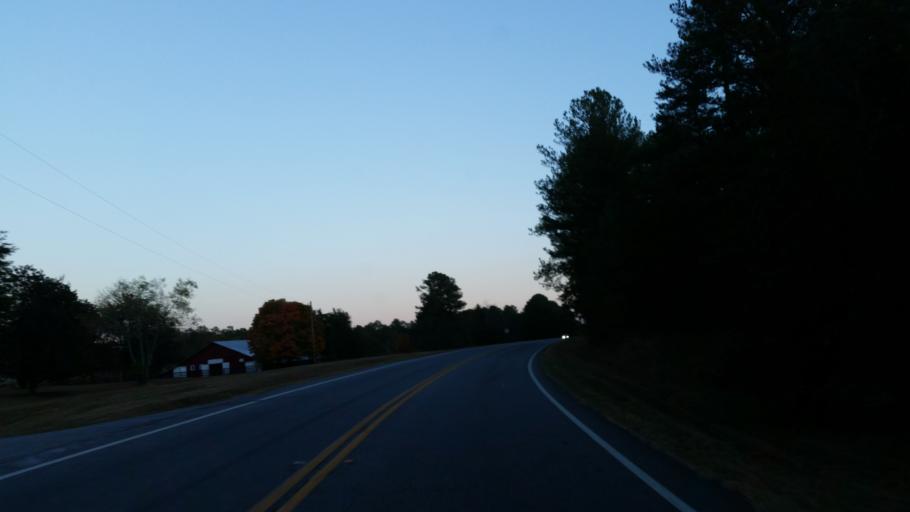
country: US
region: Georgia
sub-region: Gordon County
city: Calhoun
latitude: 34.5881
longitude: -85.0065
